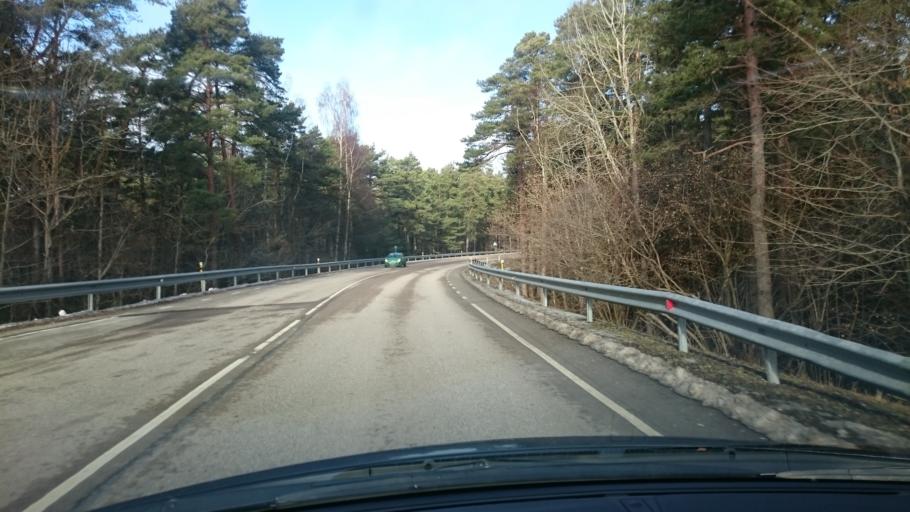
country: EE
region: Harju
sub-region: Keila linn
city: Keila
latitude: 59.4065
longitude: 24.2971
